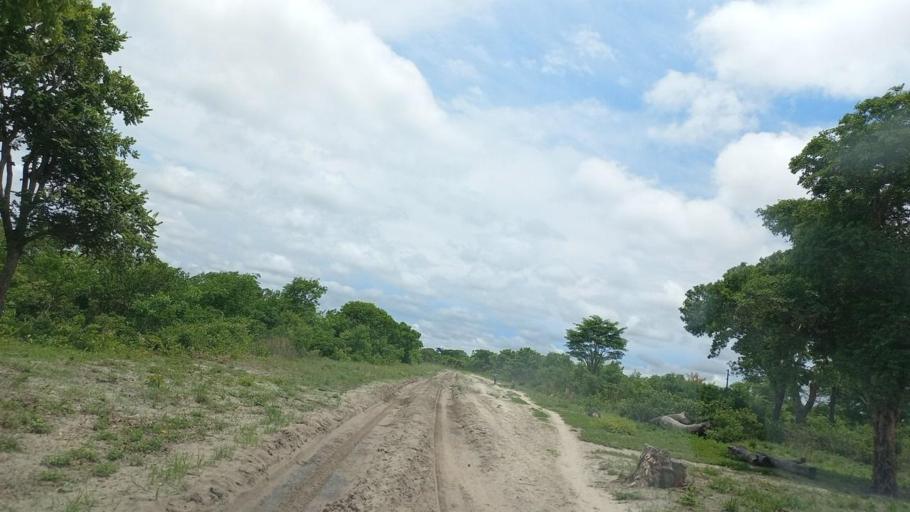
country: ZM
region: North-Western
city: Kabompo
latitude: -13.1811
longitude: 23.9493
